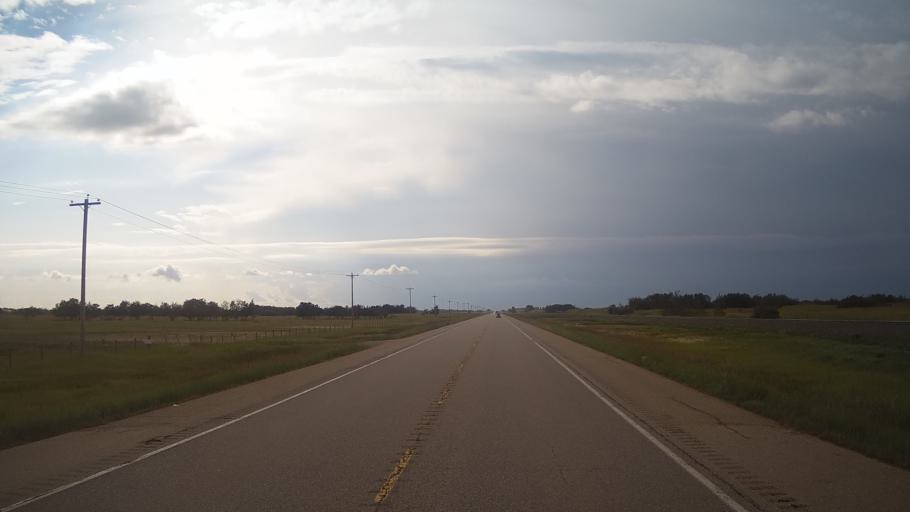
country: CA
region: Alberta
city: Viking
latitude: 53.1465
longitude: -111.9573
